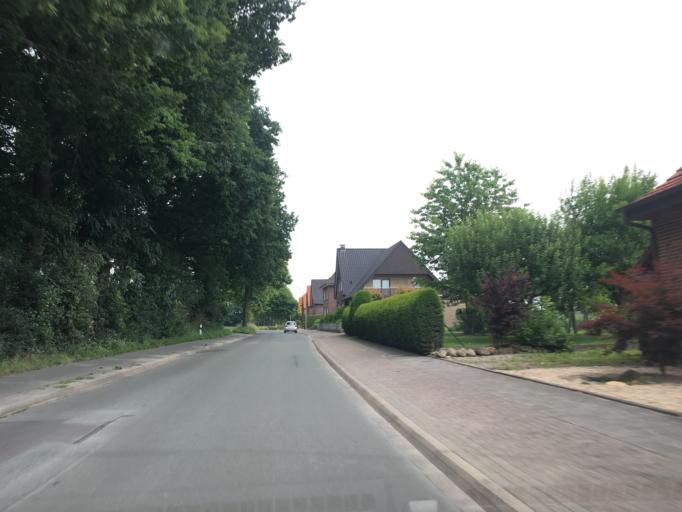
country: DE
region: North Rhine-Westphalia
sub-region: Regierungsbezirk Munster
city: Laer
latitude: 52.1026
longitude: 7.3952
